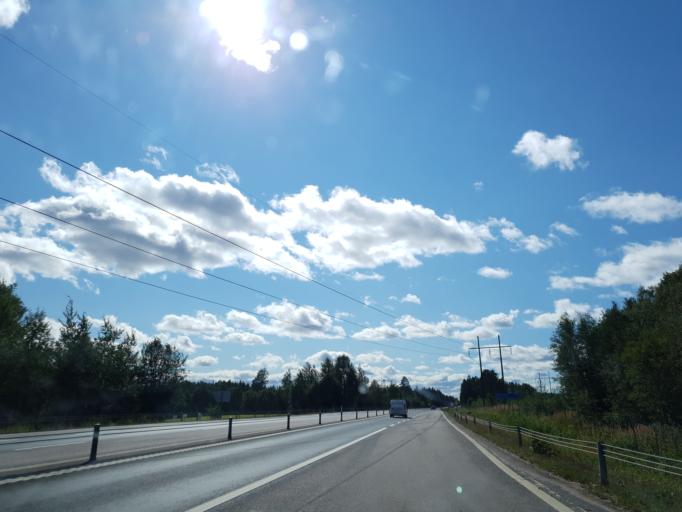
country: SE
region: Vaesterbotten
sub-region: Nordmalings Kommun
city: Nordmaling
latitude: 63.5344
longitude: 19.3996
